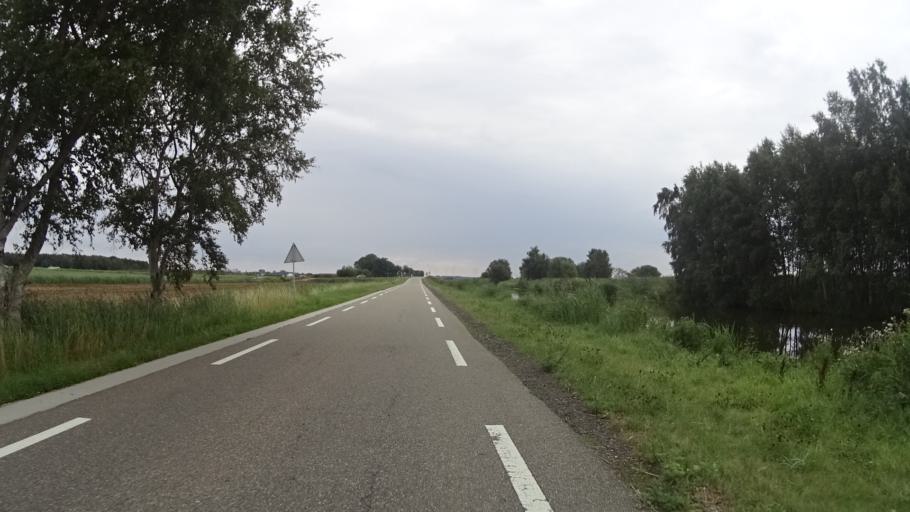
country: NL
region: Groningen
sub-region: Gemeente Slochteren
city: Slochteren
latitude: 53.2342
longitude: 6.7430
